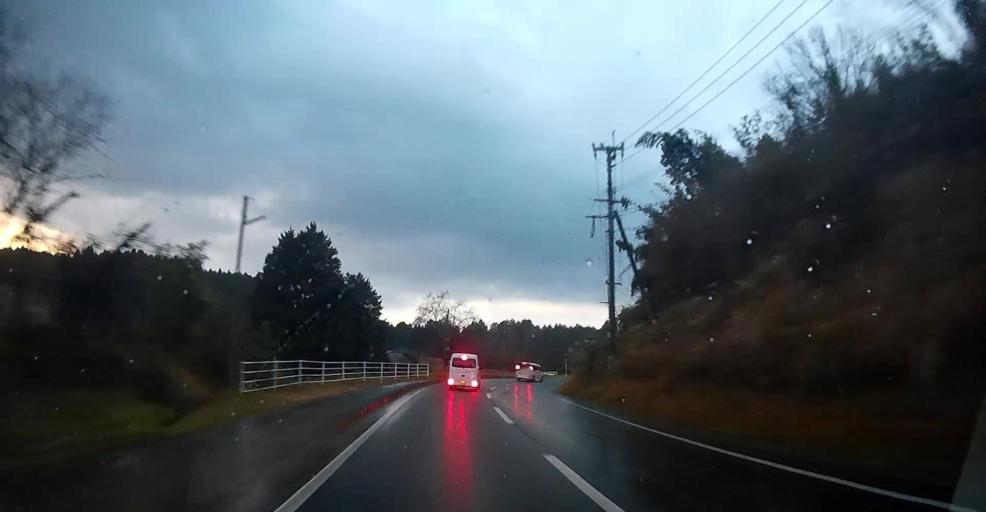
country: JP
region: Kumamoto
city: Ozu
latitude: 32.8340
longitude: 130.9159
